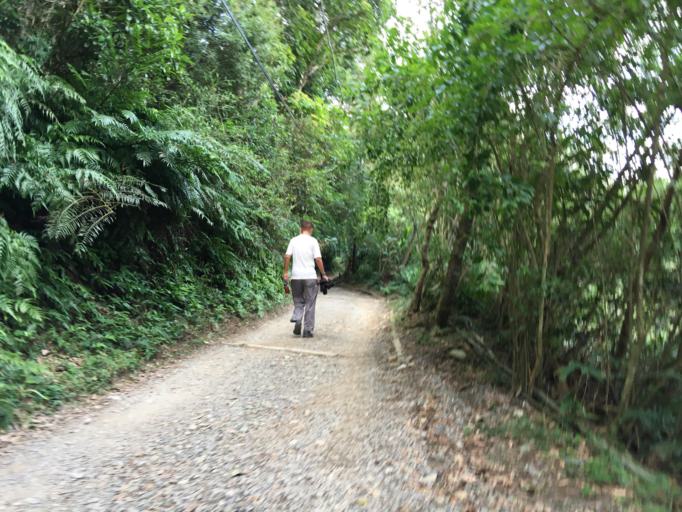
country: TW
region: Taiwan
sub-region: Yilan
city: Yilan
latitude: 24.8405
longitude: 121.7761
